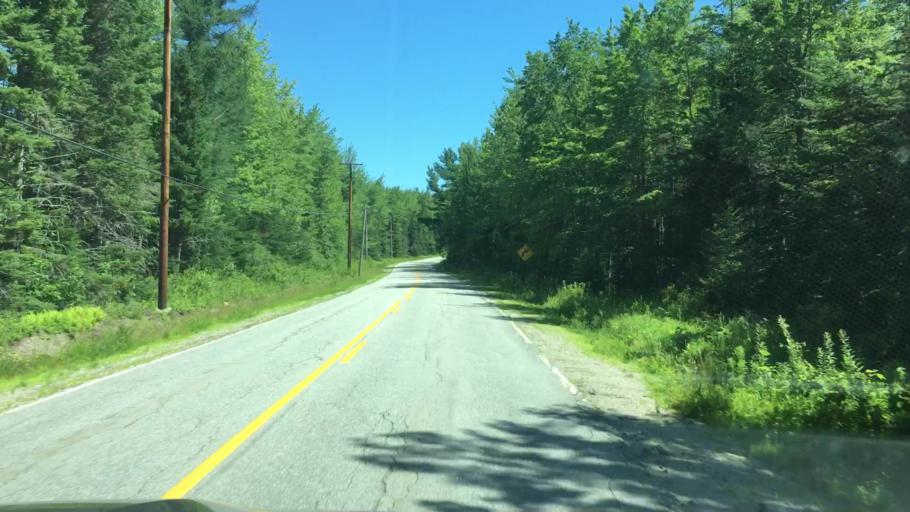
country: US
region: Maine
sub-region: Hancock County
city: Penobscot
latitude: 44.4714
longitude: -68.7025
